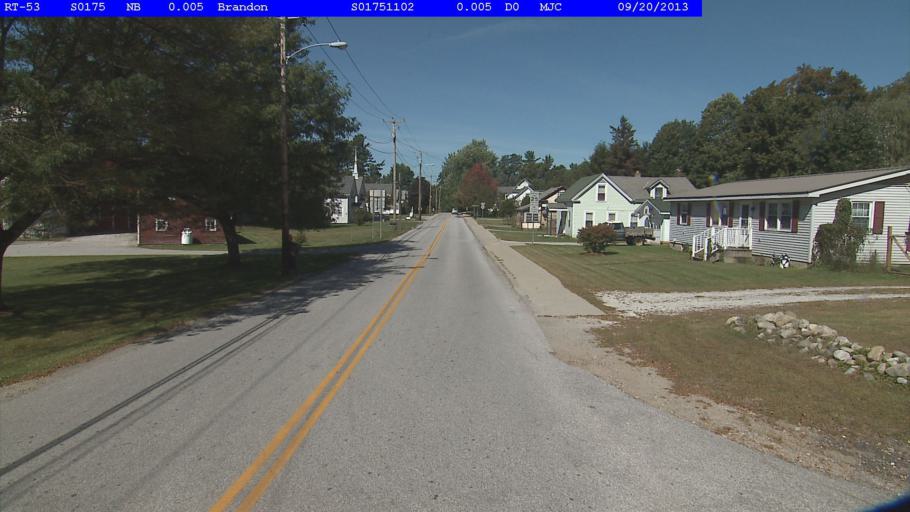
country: US
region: Vermont
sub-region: Rutland County
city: Brandon
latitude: 43.8273
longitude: -73.0531
